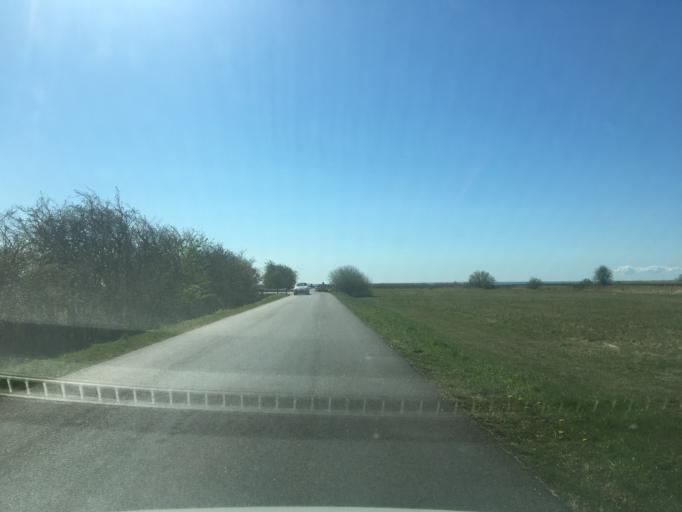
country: DK
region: Capital Region
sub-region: Dragor Kommune
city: Dragor
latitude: 55.5795
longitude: 12.6400
